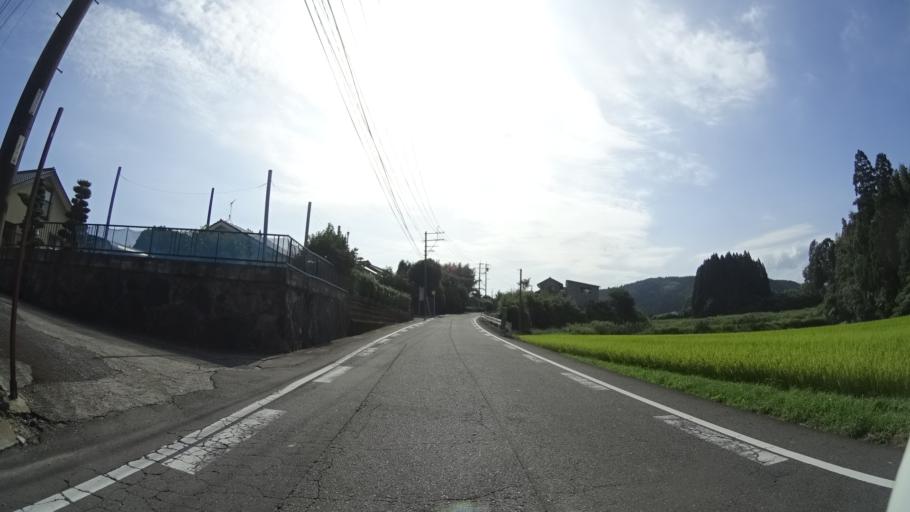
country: JP
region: Kagoshima
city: Okuchi-shinohara
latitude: 32.0446
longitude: 130.7715
